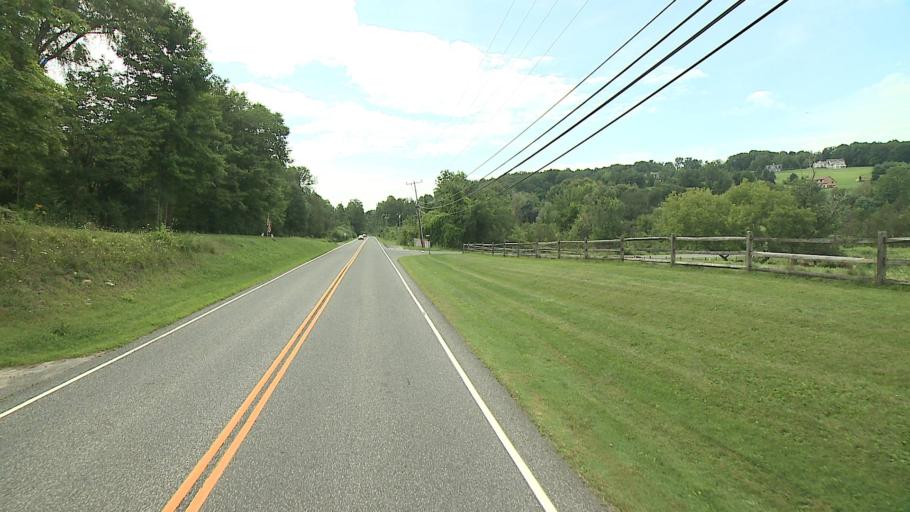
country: US
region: Connecticut
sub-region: Fairfield County
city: Sherman
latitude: 41.6097
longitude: -73.5022
